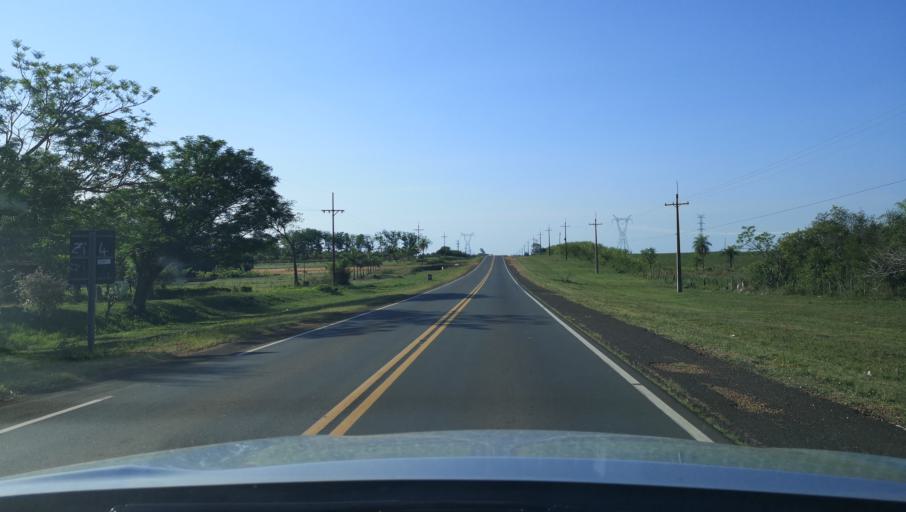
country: PY
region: Misiones
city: Santa Maria
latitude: -26.7985
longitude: -57.0223
